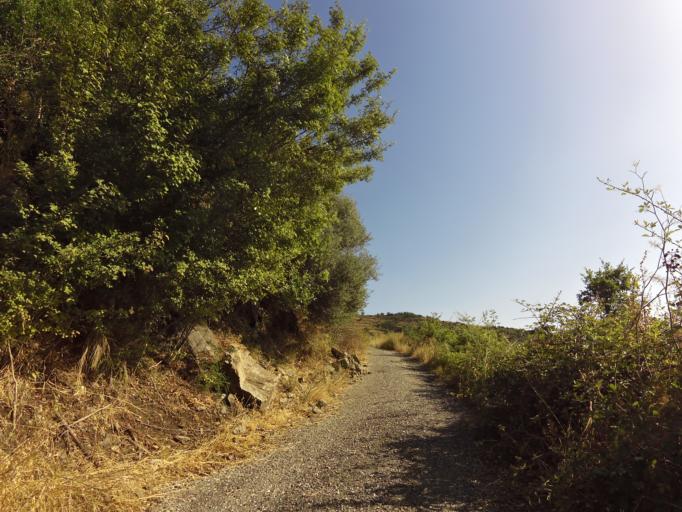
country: IT
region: Calabria
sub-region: Provincia di Reggio Calabria
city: Bivongi
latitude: 38.4956
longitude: 16.4590
